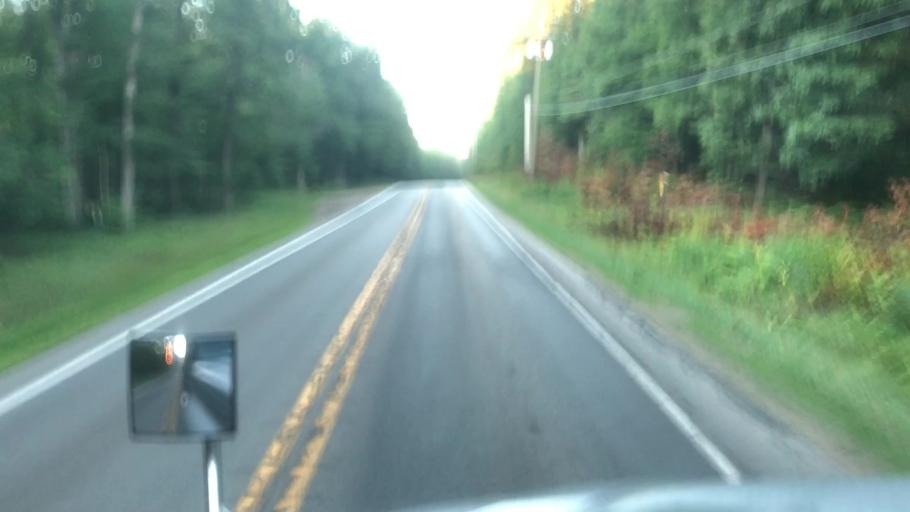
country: US
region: Pennsylvania
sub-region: Venango County
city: Hasson Heights
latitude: 41.5156
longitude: -79.6199
